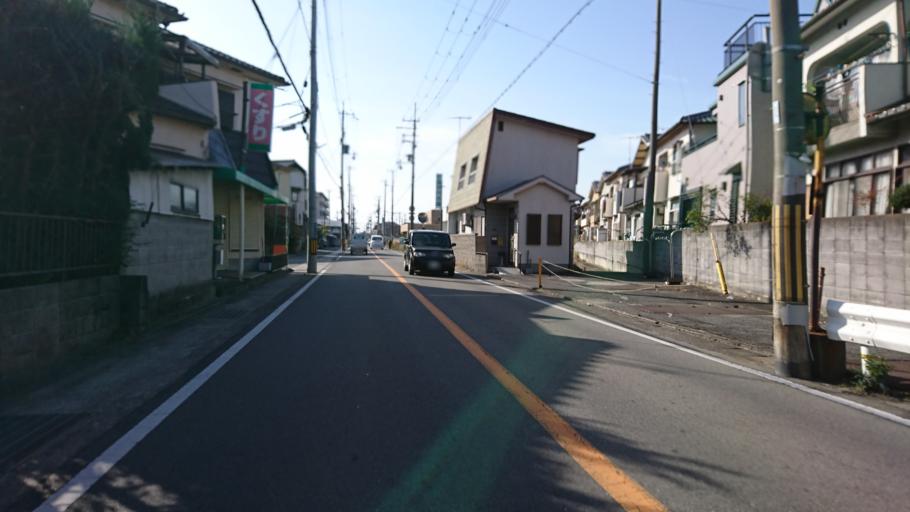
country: JP
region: Hyogo
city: Kakogawacho-honmachi
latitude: 34.7214
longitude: 134.8635
